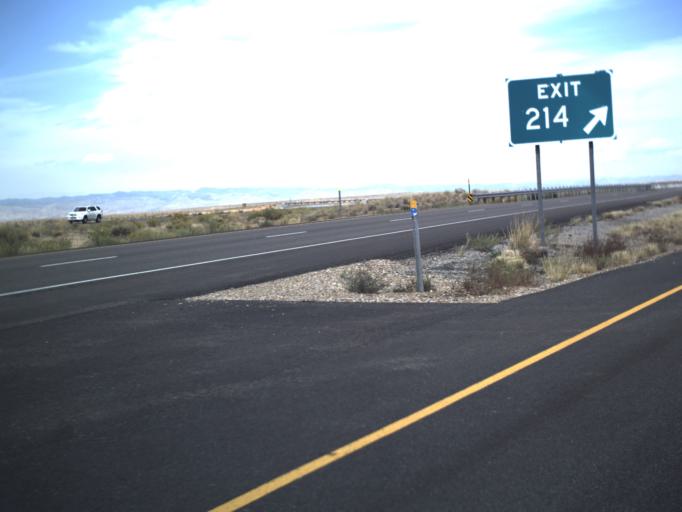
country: US
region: Colorado
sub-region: Mesa County
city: Loma
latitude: 39.0357
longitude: -109.2845
